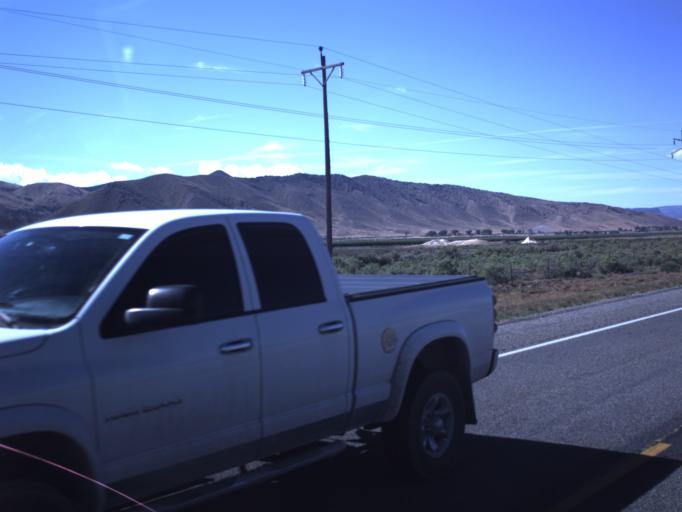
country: US
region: Utah
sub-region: Sevier County
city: Salina
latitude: 38.9997
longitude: -111.8417
